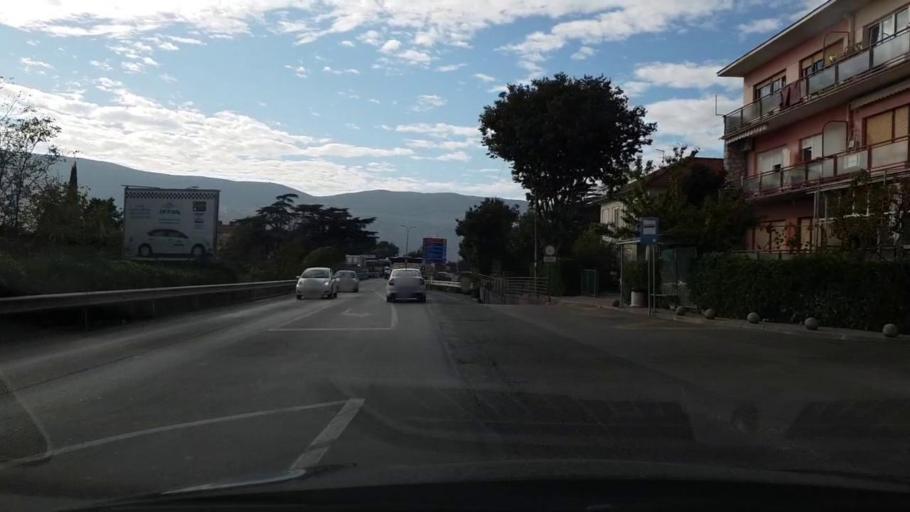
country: ME
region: Herceg Novi
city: Herceg-Novi
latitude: 42.4532
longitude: 18.5357
